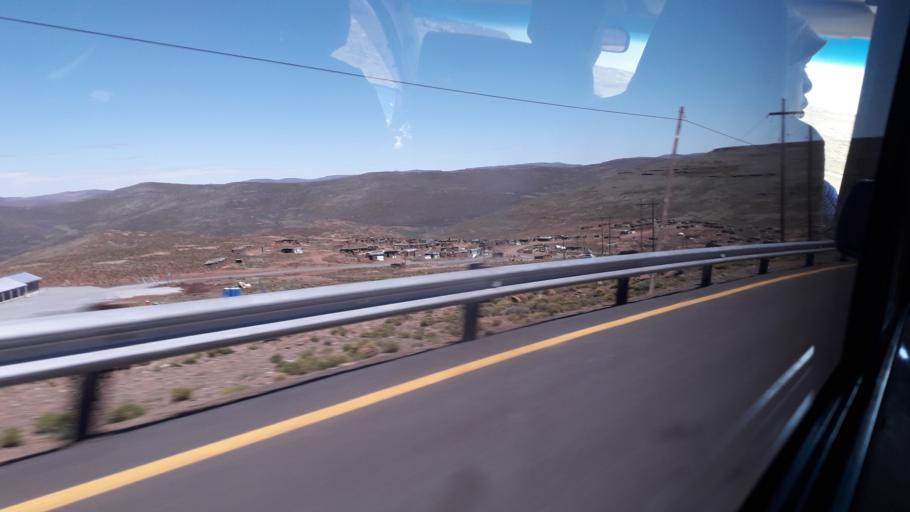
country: LS
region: Mokhotlong
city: Mokhotlong
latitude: -29.0166
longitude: 28.8476
